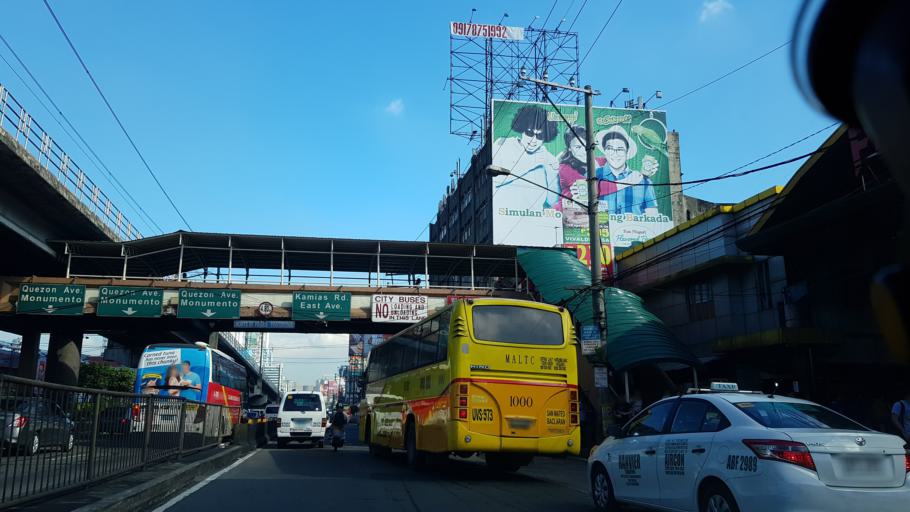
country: PH
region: Metro Manila
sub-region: Quezon City
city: Quezon City
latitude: 14.6234
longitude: 121.0494
